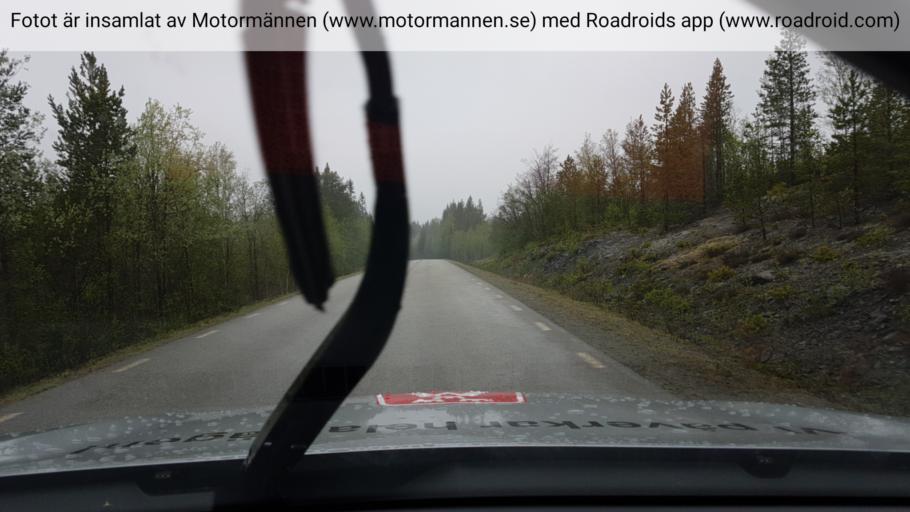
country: SE
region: Jaemtland
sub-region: Bergs Kommun
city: Hoverberg
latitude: 63.0382
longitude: 14.0181
